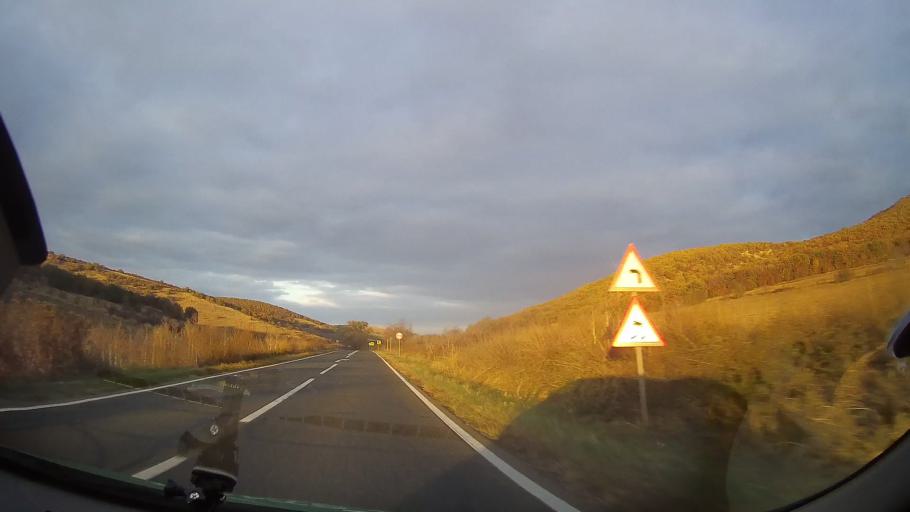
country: RO
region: Tulcea
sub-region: Comuna Ciucurova
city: Ciucurova
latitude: 44.9565
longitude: 28.5162
